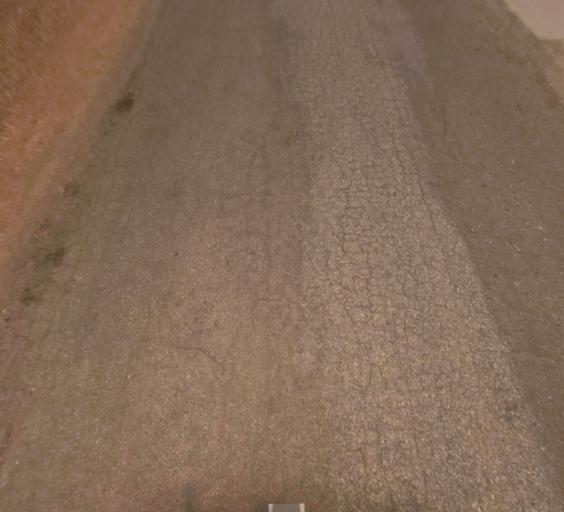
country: US
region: California
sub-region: Madera County
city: Coarsegold
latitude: 37.2184
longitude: -119.6737
